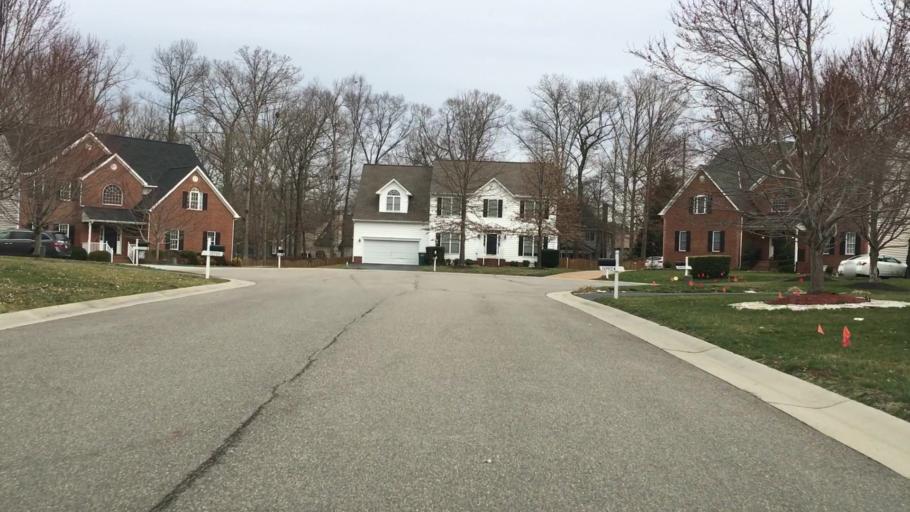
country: US
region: Virginia
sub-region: Henrico County
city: Short Pump
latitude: 37.6564
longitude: -77.5688
